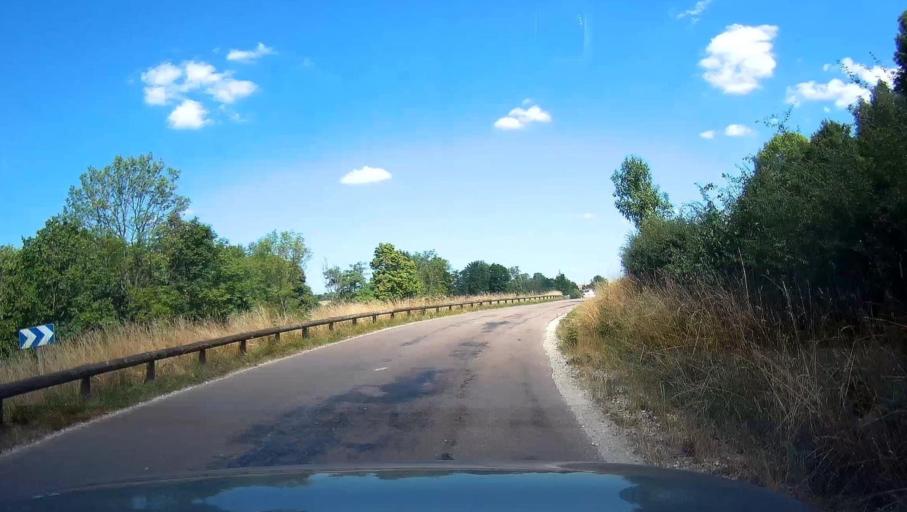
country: FR
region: Champagne-Ardenne
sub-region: Departement de la Haute-Marne
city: Langres
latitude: 47.8609
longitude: 5.3697
